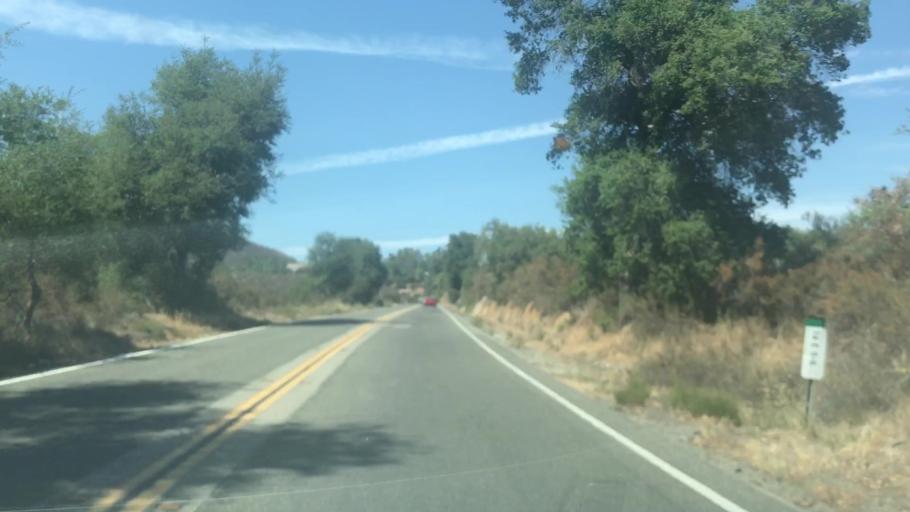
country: US
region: California
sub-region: Riverside County
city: Lakeland Village
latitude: 33.6409
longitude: -117.4216
